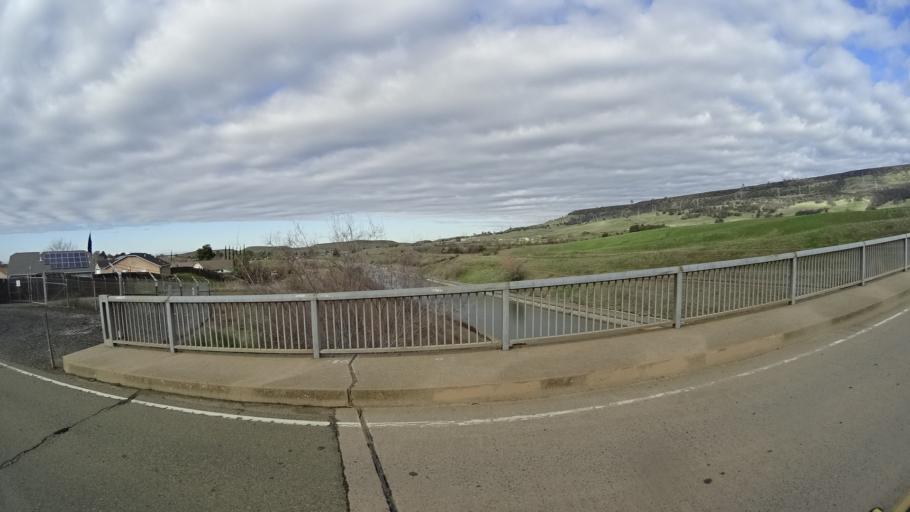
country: US
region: California
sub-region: Butte County
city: Oroville
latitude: 39.5282
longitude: -121.5561
